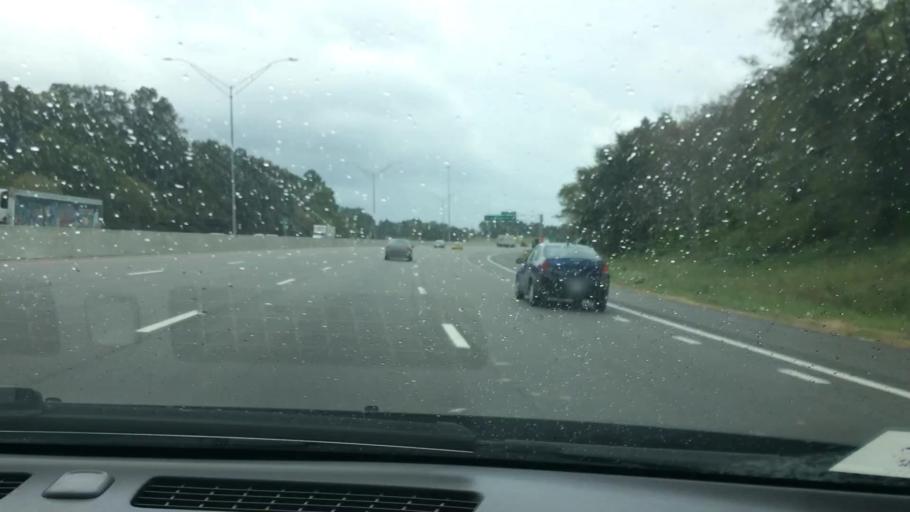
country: US
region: North Carolina
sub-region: Wake County
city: Raleigh
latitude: 35.7557
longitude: -78.6185
